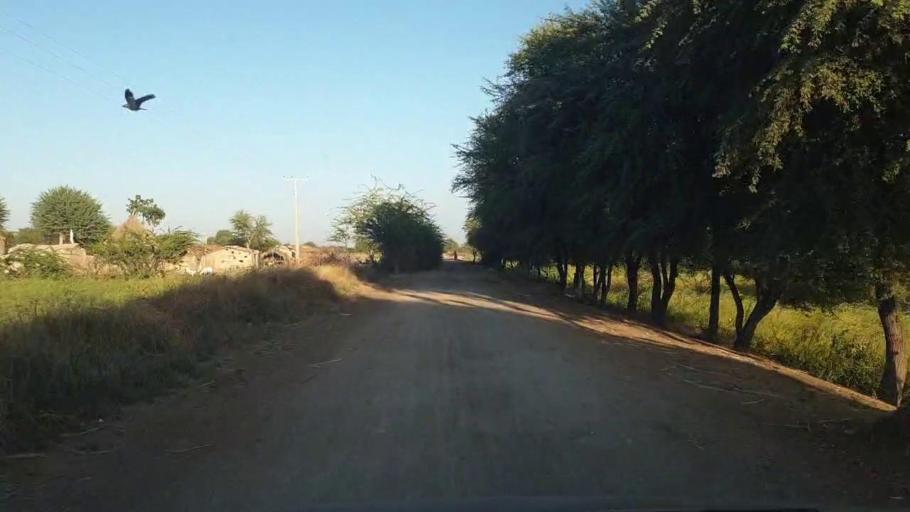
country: PK
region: Sindh
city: Dhoro Naro
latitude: 25.3749
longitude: 69.5628
